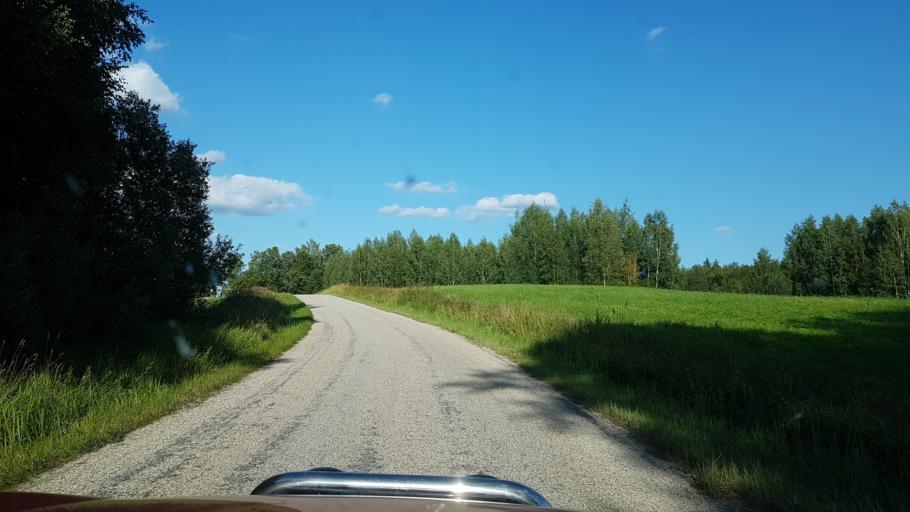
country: EE
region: Vorumaa
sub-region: Voru linn
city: Voru
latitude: 57.8912
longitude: 27.1089
